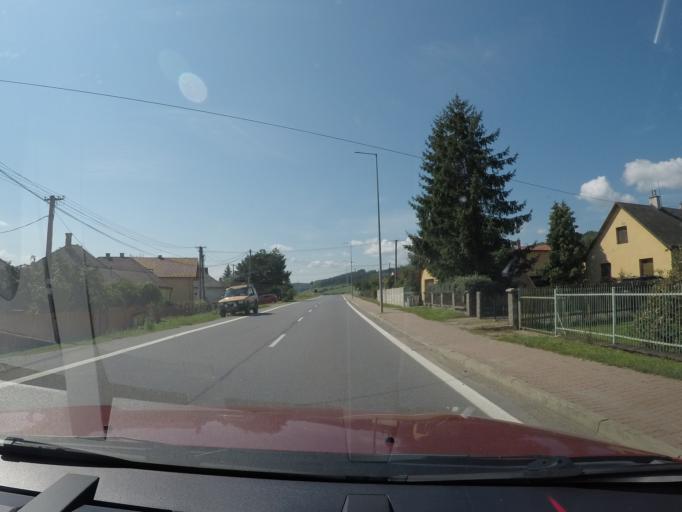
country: SK
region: Presovsky
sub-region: Okres Presov
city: Presov
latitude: 48.9229
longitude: 21.2413
